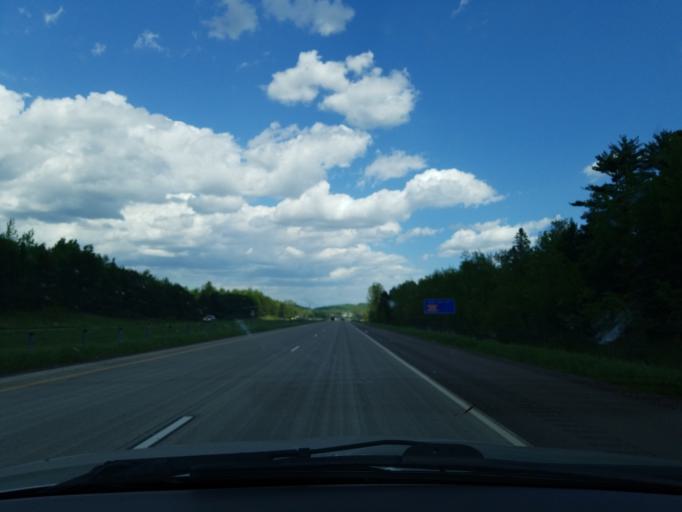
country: US
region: Minnesota
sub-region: Carlton County
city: Esko
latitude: 46.7002
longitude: -92.3194
